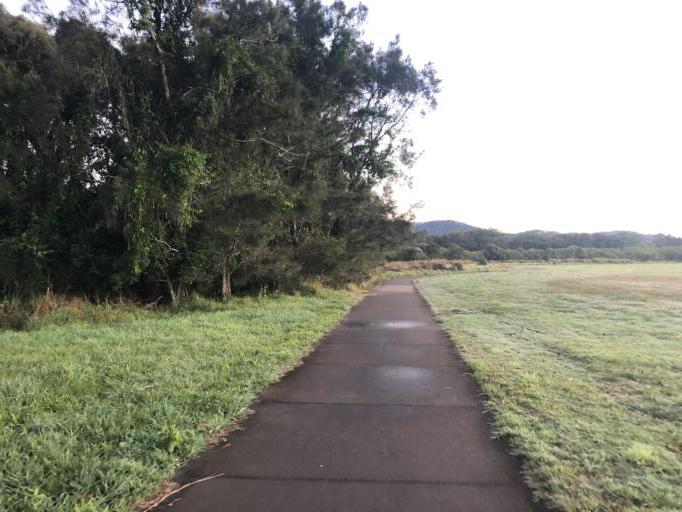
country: AU
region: New South Wales
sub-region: Coffs Harbour
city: Coffs Harbour
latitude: -30.3010
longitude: 153.1346
